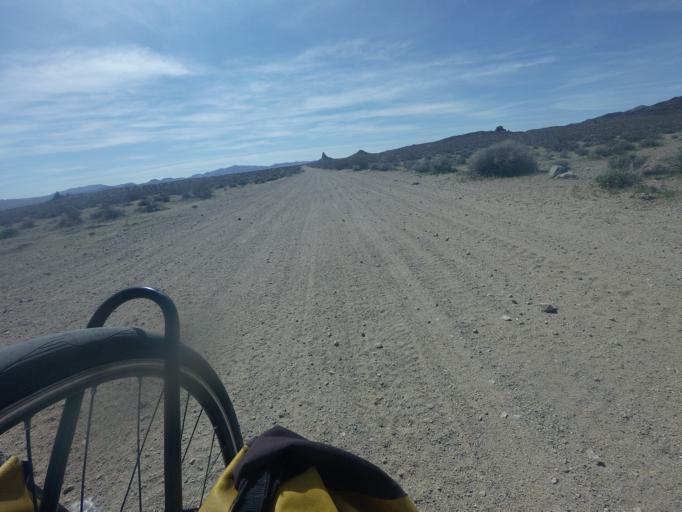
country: US
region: California
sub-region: San Bernardino County
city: Searles Valley
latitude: 35.5803
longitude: -117.4284
